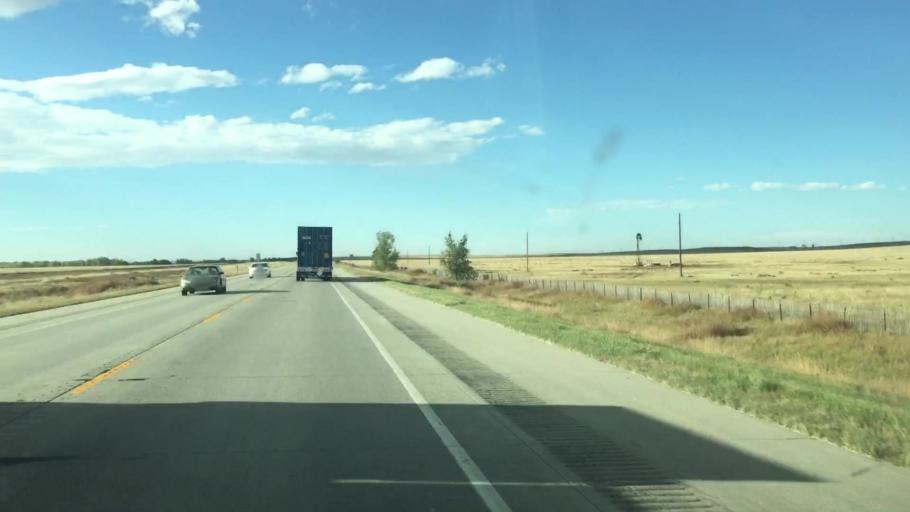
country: US
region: Colorado
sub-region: Lincoln County
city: Limon
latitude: 39.2200
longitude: -103.6064
